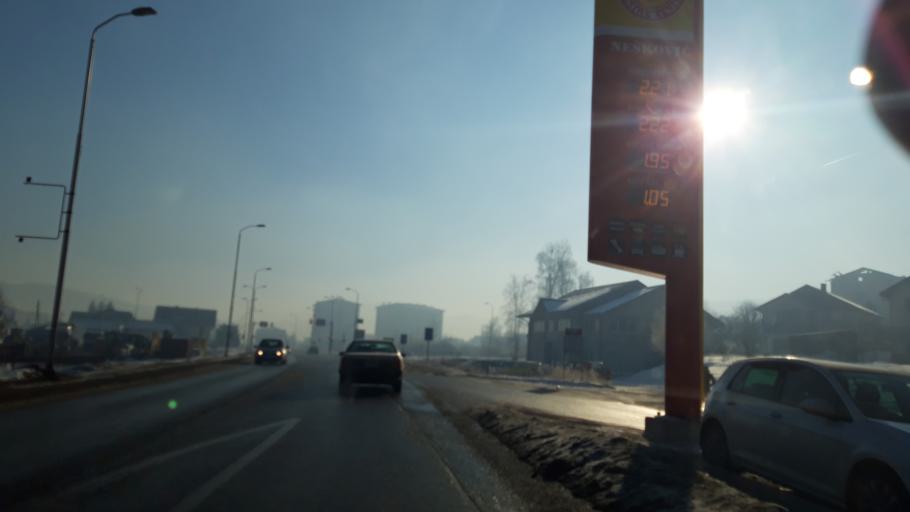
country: BA
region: Republika Srpska
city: Pale
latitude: 43.8138
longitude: 18.5641
